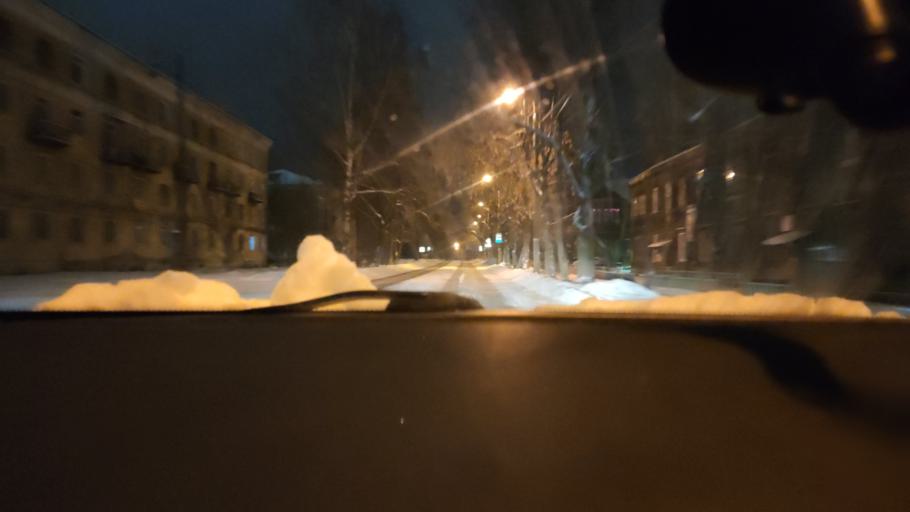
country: RU
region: Perm
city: Krasnokamsk
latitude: 58.0864
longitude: 55.7641
